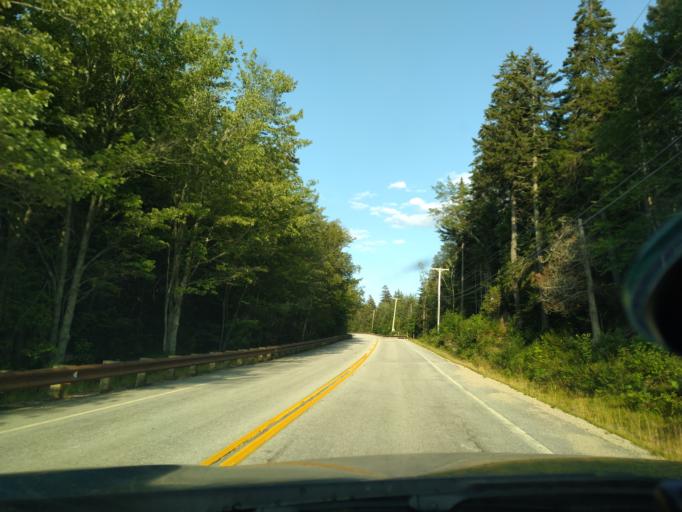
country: US
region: Maine
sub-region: Hancock County
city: Gouldsboro
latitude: 44.3937
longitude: -68.0719
